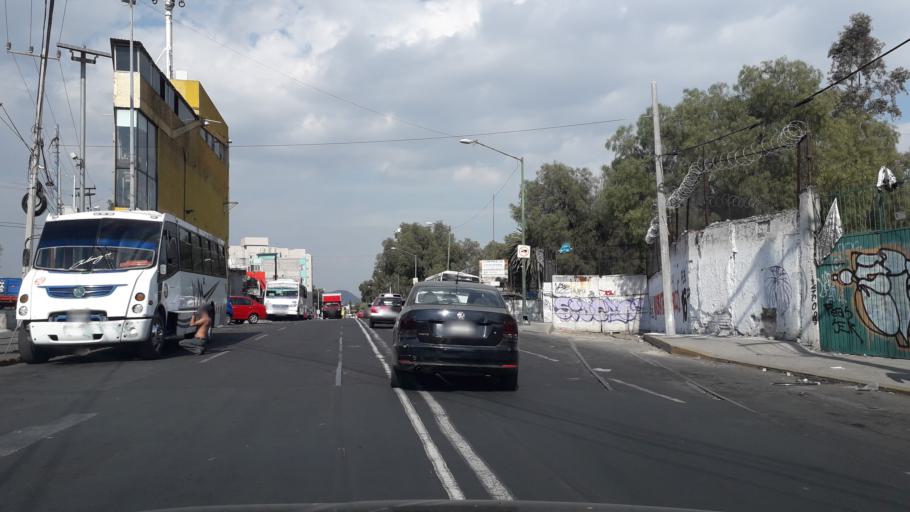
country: MX
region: Mexico City
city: Gustavo A. Madero
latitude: 19.4900
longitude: -99.1003
